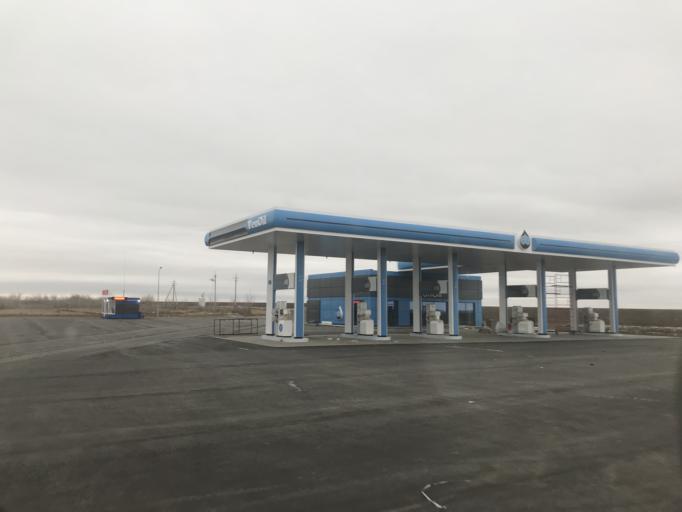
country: KZ
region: Batys Qazaqstan
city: Peremetnoe
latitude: 51.6472
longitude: 51.0117
